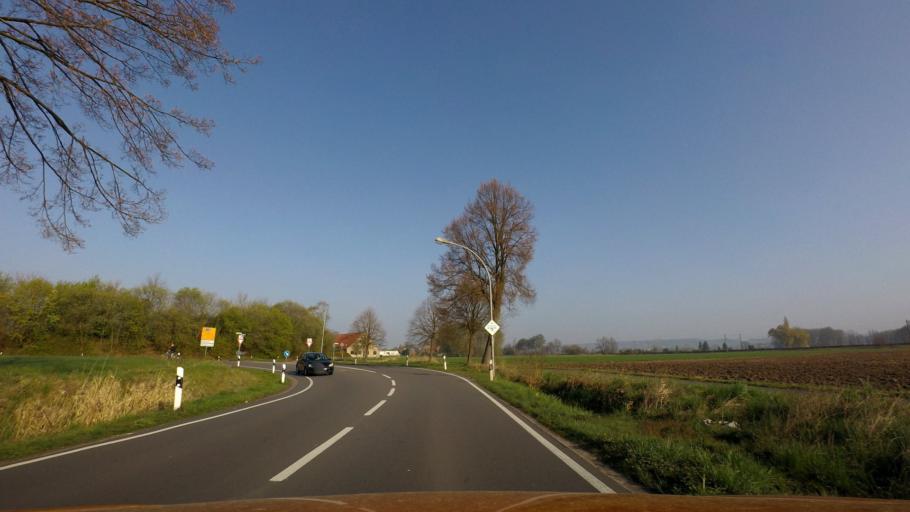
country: DE
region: Lower Saxony
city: Melle
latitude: 52.2107
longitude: 8.3239
